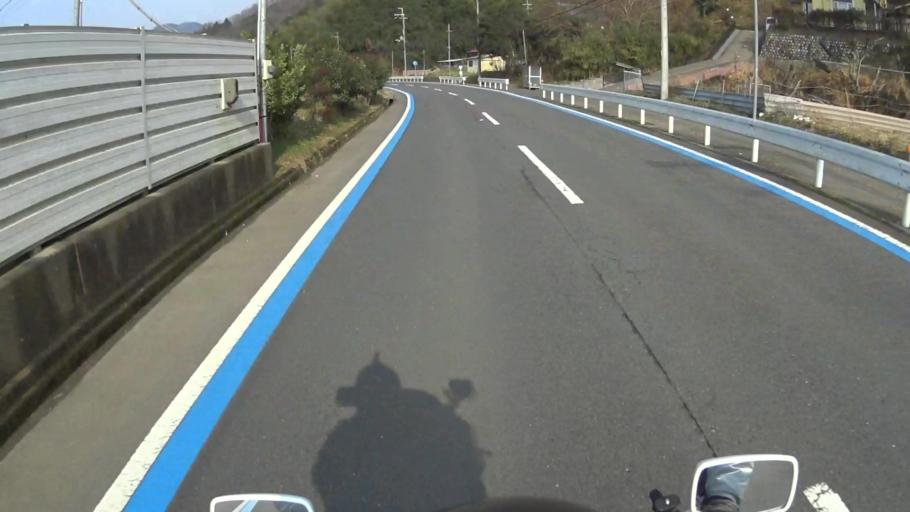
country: JP
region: Kyoto
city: Fukuchiyama
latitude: 35.3298
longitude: 135.1196
